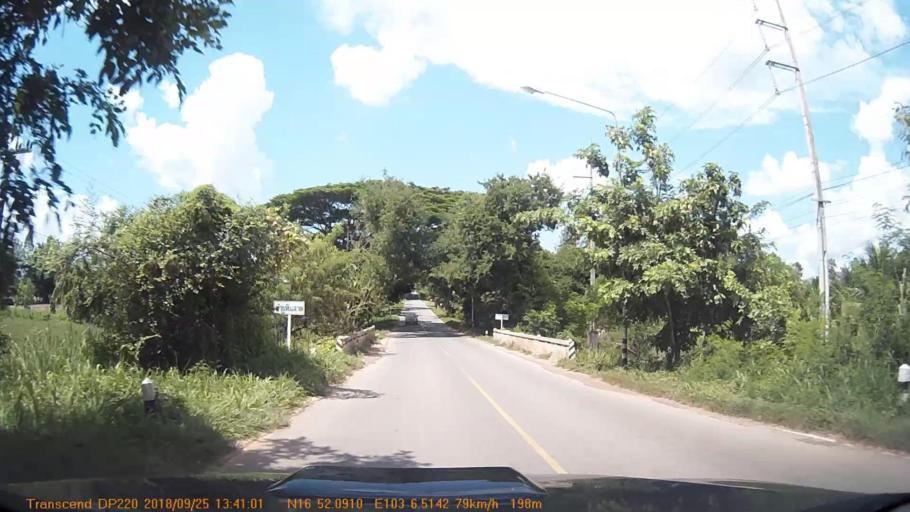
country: TH
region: Changwat Udon Thani
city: Si That
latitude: 16.8683
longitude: 103.1086
